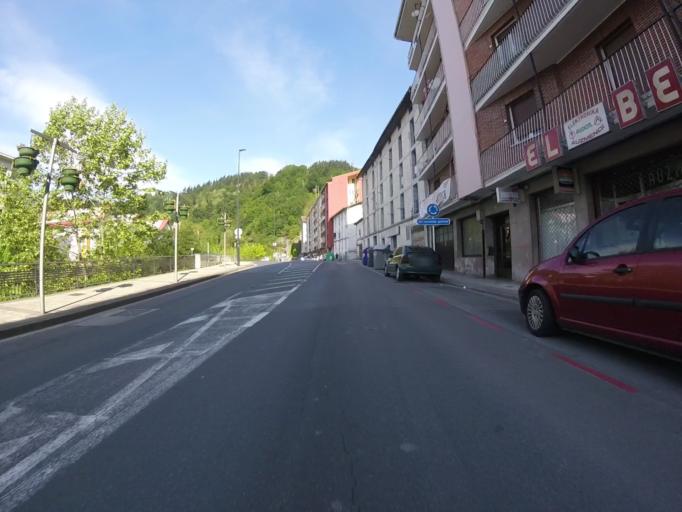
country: ES
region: Basque Country
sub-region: Provincia de Guipuzcoa
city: Villafranca de Ordizia
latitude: 43.0544
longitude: -2.1858
